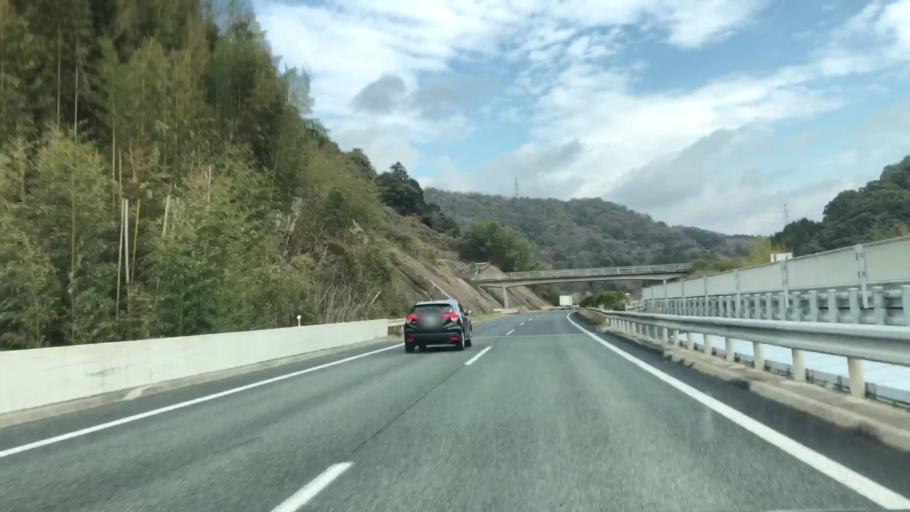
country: JP
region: Saga Prefecture
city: Kanzakimachi-kanzaki
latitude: 33.3361
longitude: 130.3278
